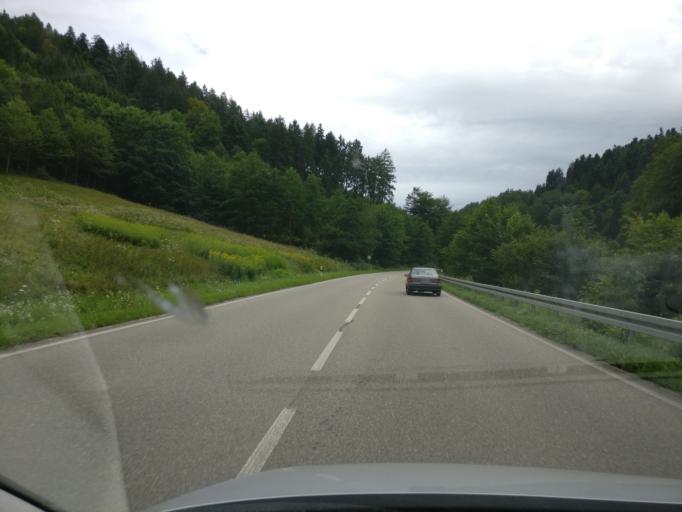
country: DE
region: Baden-Wuerttemberg
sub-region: Freiburg Region
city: Lautenbach
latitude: 48.5062
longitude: 8.1368
